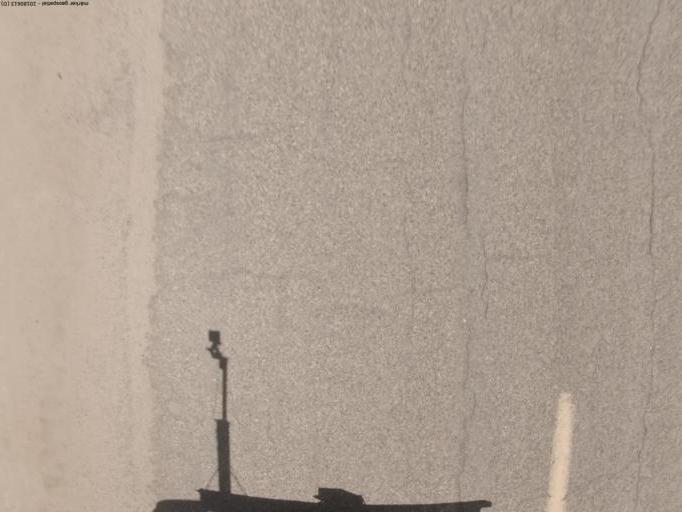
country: US
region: California
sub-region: Madera County
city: Chowchilla
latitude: 37.0772
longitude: -120.3108
